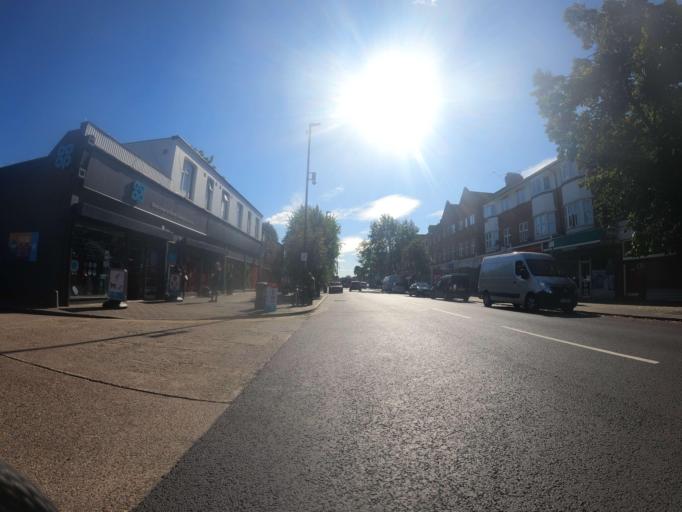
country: GB
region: England
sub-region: Greater London
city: Ealing
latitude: 51.5001
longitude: -0.3063
